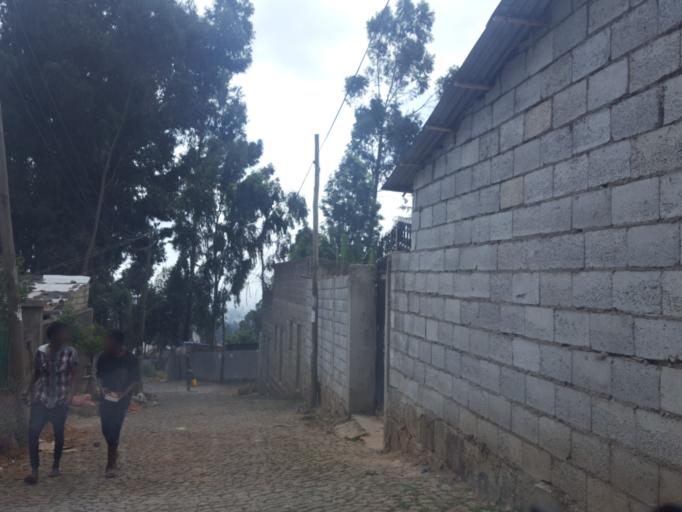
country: ET
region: Adis Abeba
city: Addis Ababa
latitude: 9.0665
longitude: 38.7454
